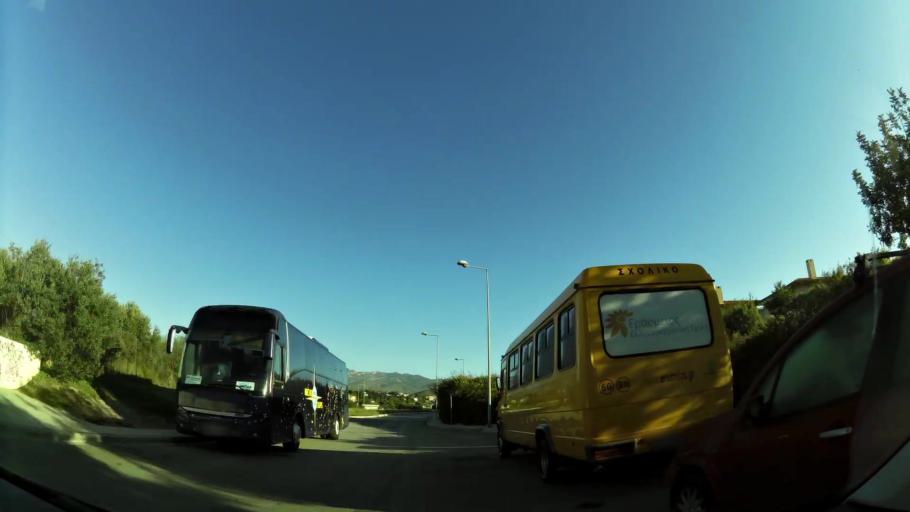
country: GR
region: Attica
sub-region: Nomarchia Anatolikis Attikis
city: Pallini
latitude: 38.0062
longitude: 23.8760
